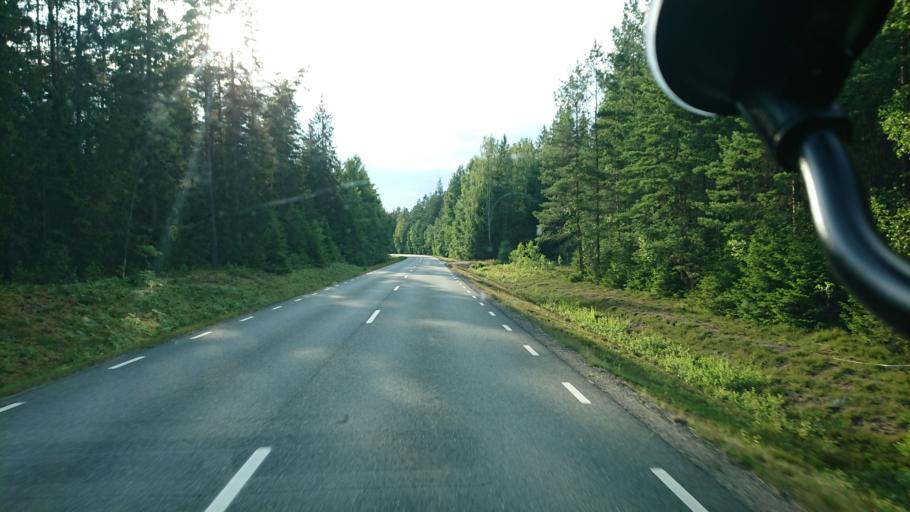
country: SE
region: Kronoberg
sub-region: Vaxjo Kommun
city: Rottne
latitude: 57.0361
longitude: 14.9230
